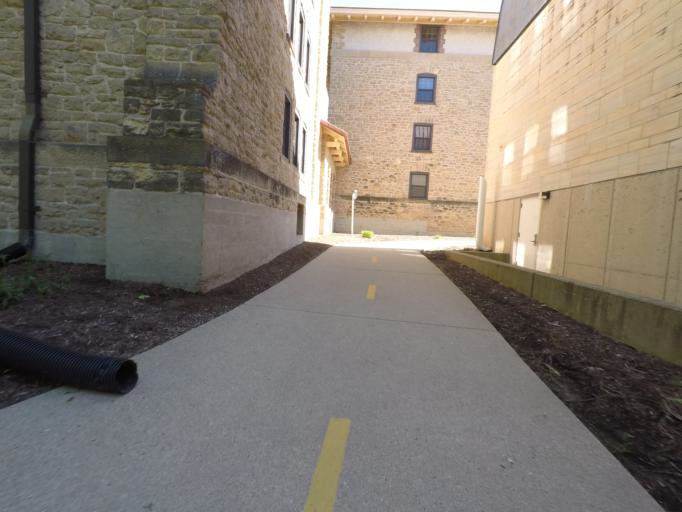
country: US
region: Wisconsin
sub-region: Dane County
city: Madison
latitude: 43.0782
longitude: -89.4122
